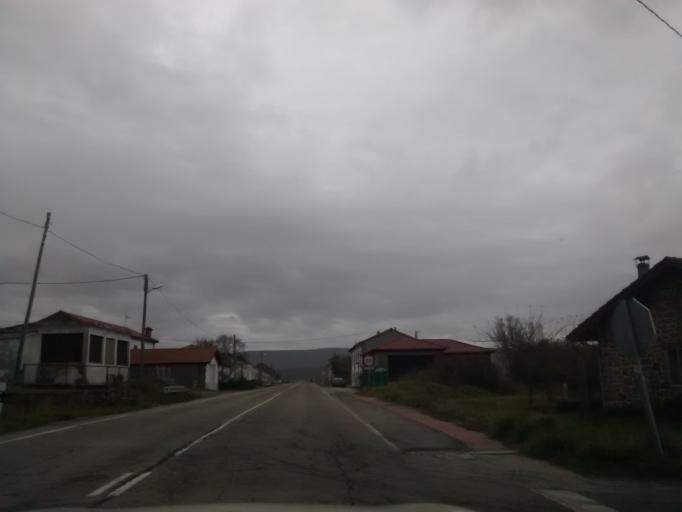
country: ES
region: Castille and Leon
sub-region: Provincia de Burgos
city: Arija
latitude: 42.9945
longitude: -3.8593
